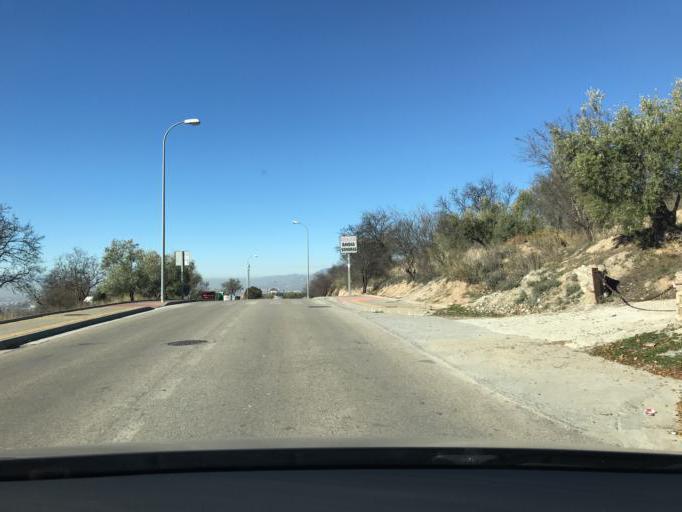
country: ES
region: Andalusia
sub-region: Provincia de Granada
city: Jun
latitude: 37.2189
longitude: -3.5820
